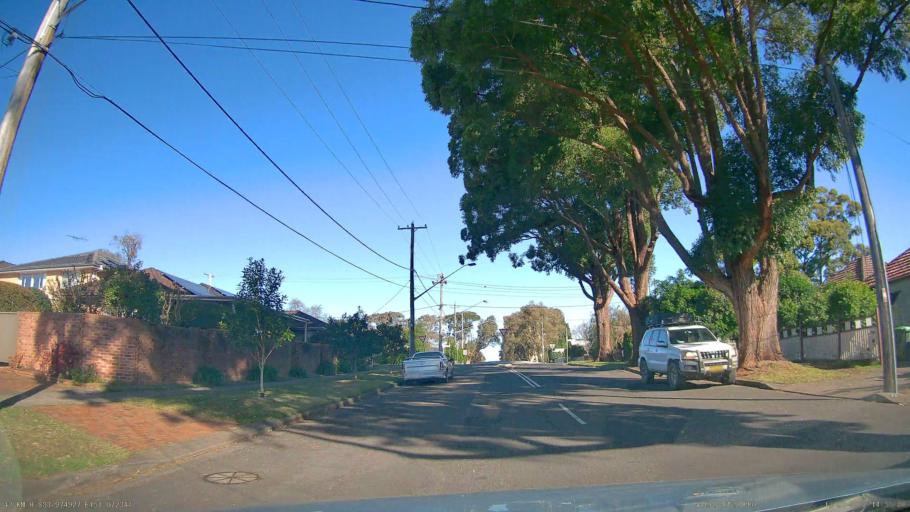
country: AU
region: New South Wales
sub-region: Hurstville
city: Oatley
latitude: -33.9751
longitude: 151.0723
